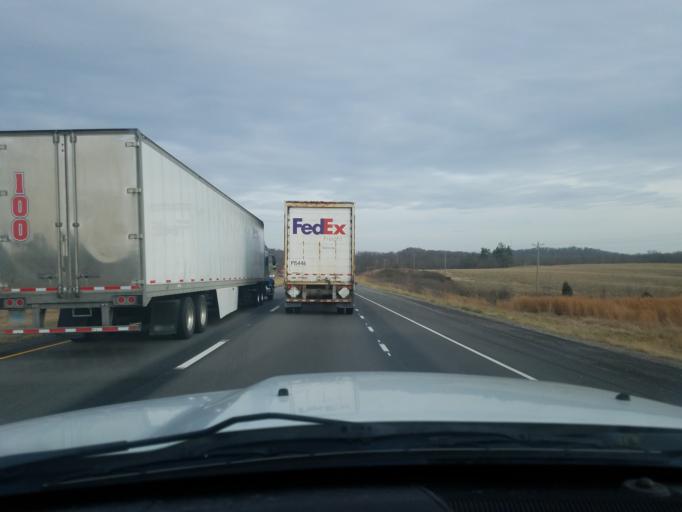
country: US
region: Indiana
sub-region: Dubois County
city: Ferdinand
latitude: 38.2052
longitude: -86.8574
